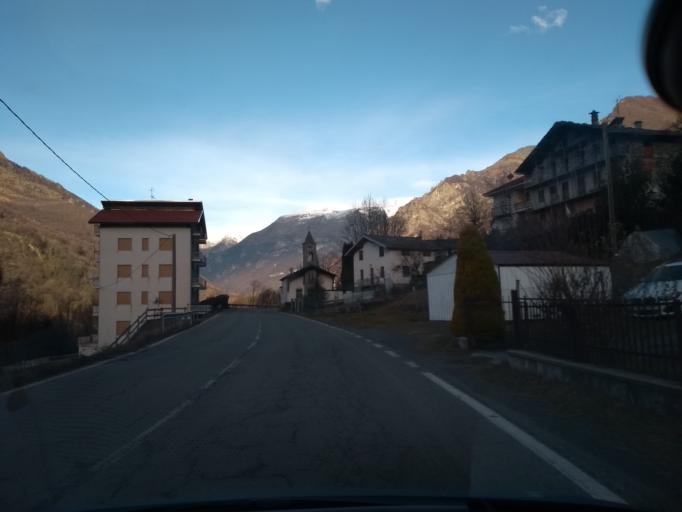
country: IT
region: Piedmont
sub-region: Provincia di Torino
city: Cantoira
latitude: 45.3308
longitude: 7.3940
